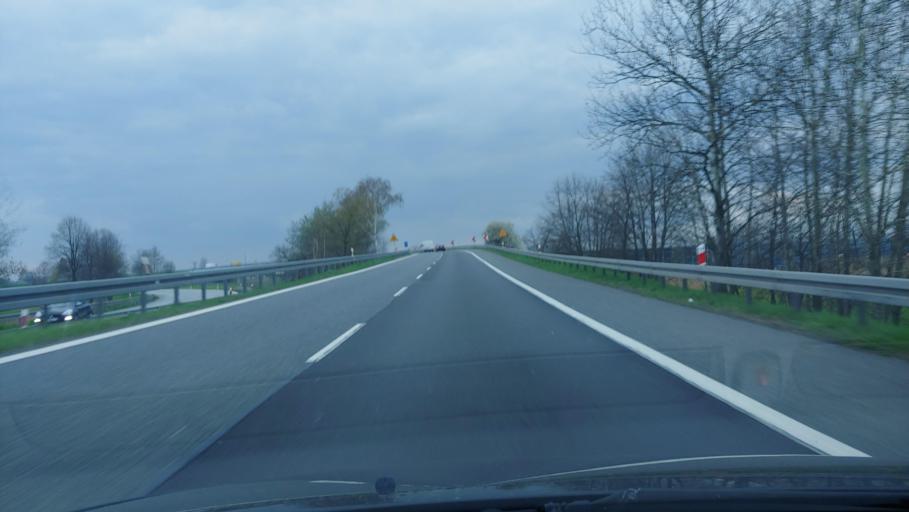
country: PL
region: Silesian Voivodeship
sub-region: Tychy
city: Cielmice
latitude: 50.1351
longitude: 19.0293
